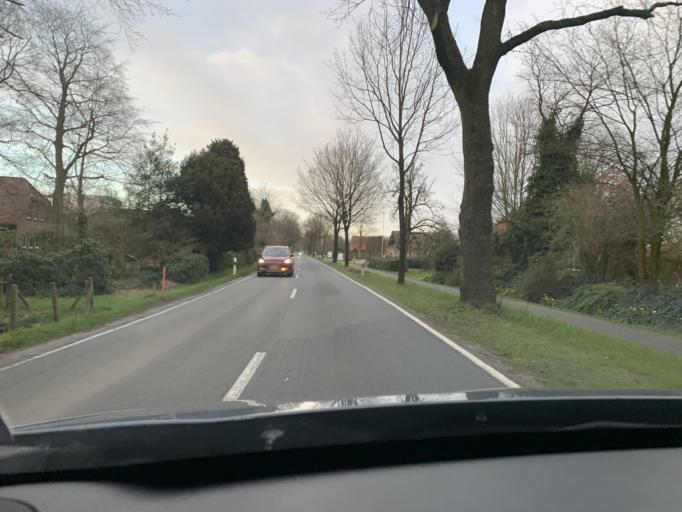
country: DE
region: Lower Saxony
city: Apen
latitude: 53.1914
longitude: 7.8671
